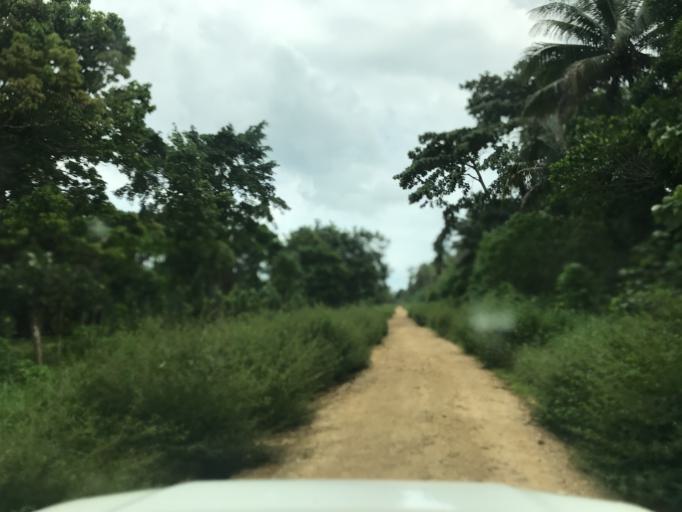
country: VU
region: Sanma
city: Port-Olry
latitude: -15.1855
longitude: 167.0266
